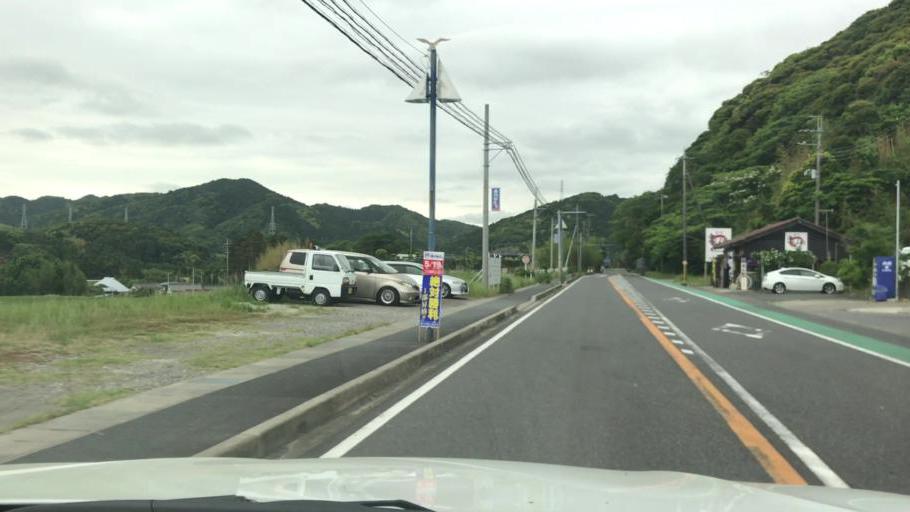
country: JP
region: Chiba
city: Kawaguchi
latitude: 35.1264
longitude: 140.0798
